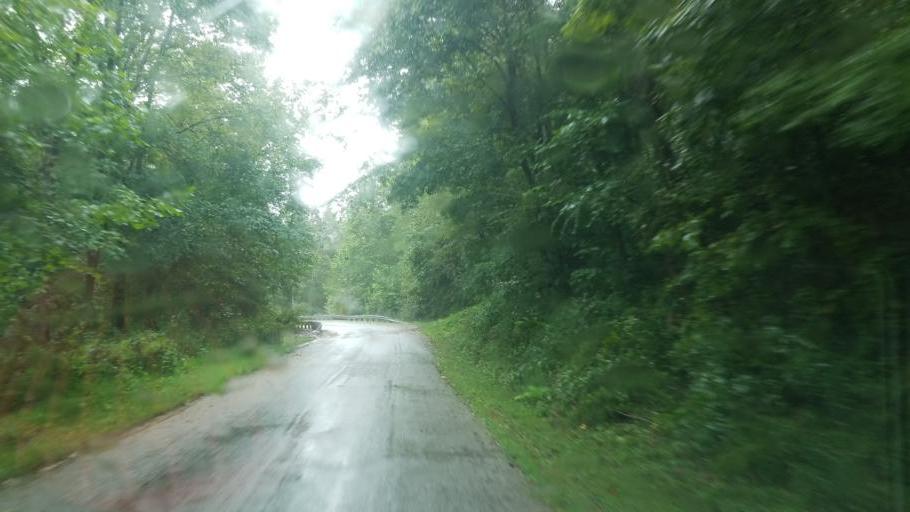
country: US
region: Kentucky
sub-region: Lewis County
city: Vanceburg
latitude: 38.7853
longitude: -83.2584
